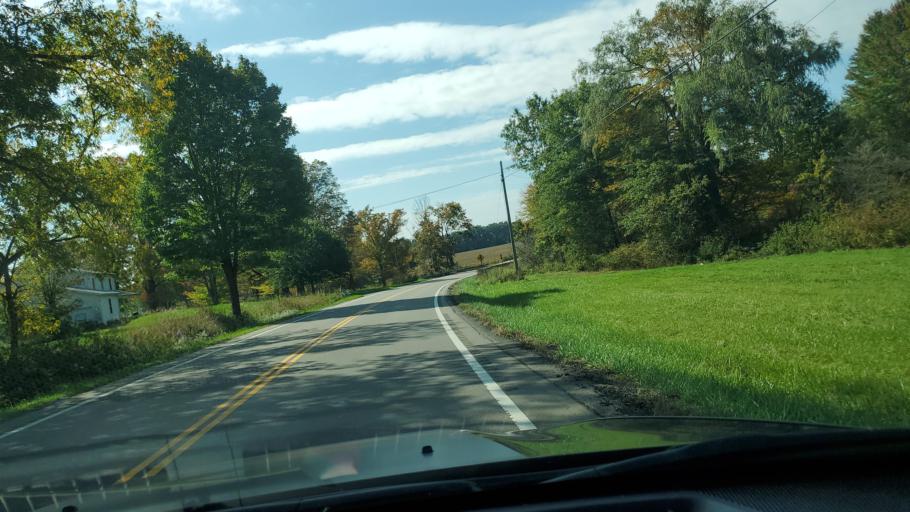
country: US
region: Ohio
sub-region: Trumbull County
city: Cortland
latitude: 41.4220
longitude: -80.6008
